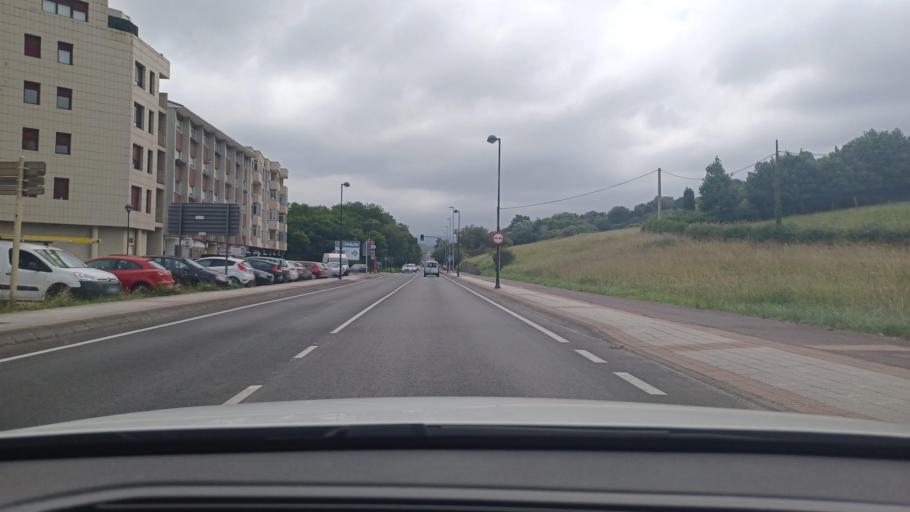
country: ES
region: Asturias
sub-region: Province of Asturias
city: Castrillon
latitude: 43.5705
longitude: -5.9612
